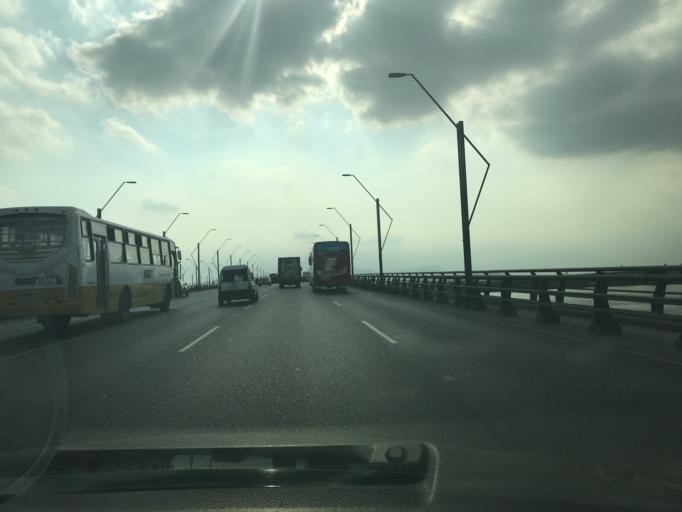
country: EC
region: Guayas
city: Eloy Alfaro
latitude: -2.1527
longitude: -79.8702
